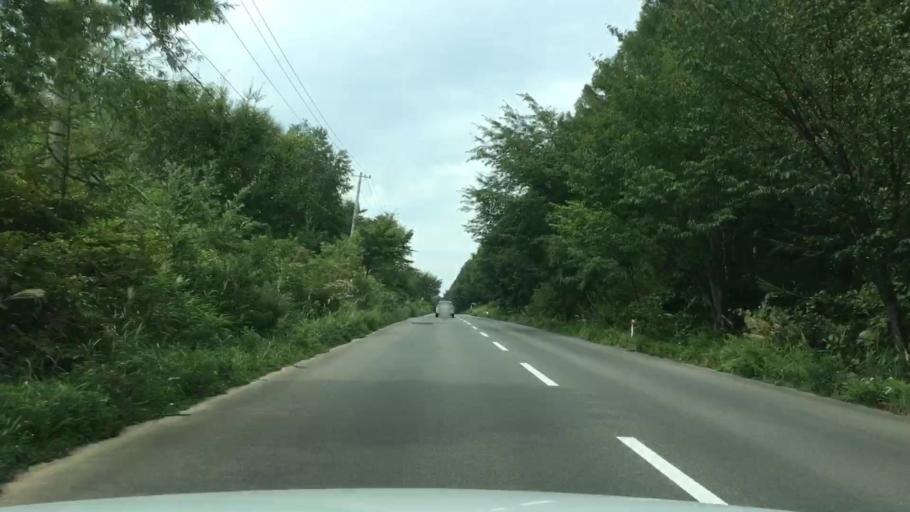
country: JP
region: Aomori
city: Shimokizukuri
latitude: 40.7135
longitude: 140.3229
